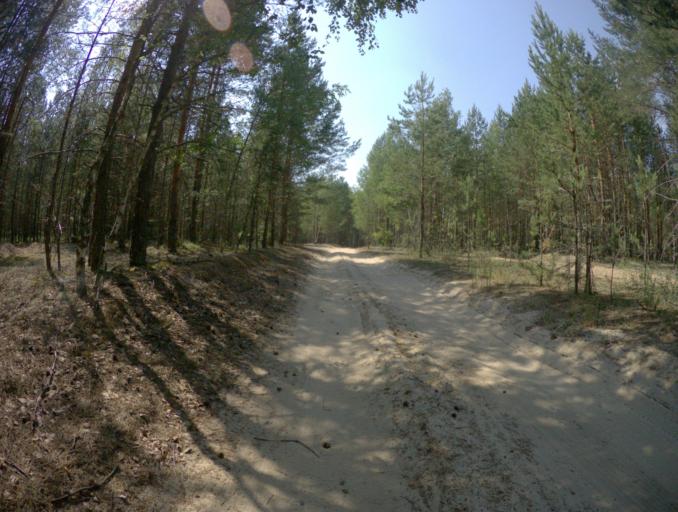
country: RU
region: Ivanovo
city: Talitsy
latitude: 56.4056
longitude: 42.3554
